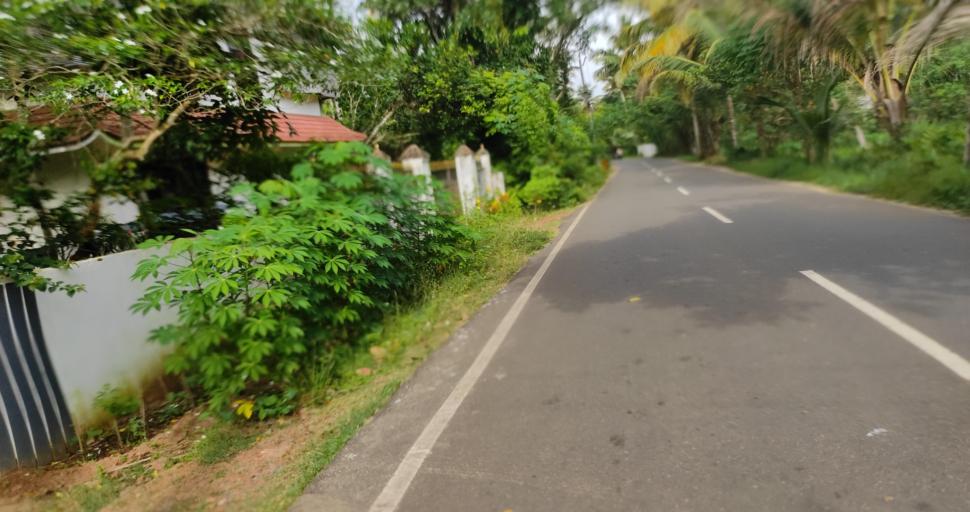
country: IN
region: Kerala
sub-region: Alappuzha
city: Vayalar
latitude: 9.6550
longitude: 76.3042
